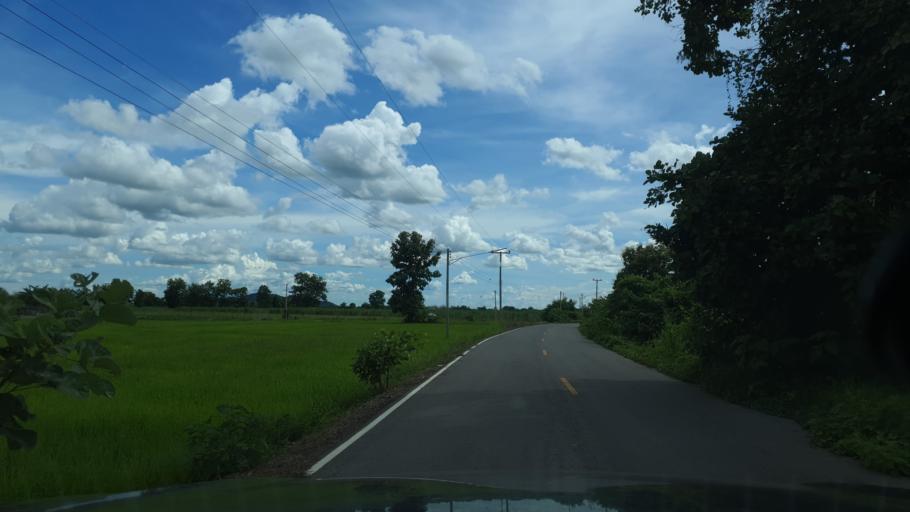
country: TH
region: Sukhothai
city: Thung Saliam
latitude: 17.3454
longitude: 99.6394
